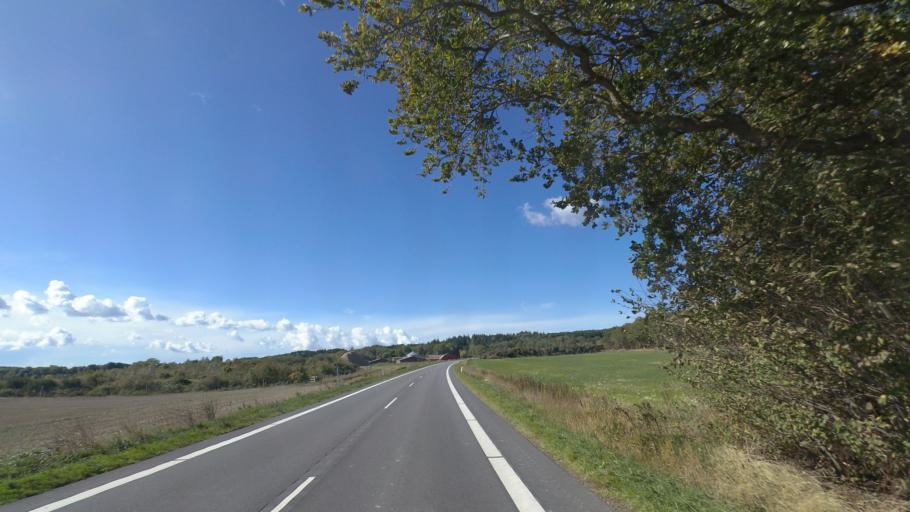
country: DK
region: Capital Region
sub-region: Bornholm Kommune
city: Nexo
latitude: 55.0630
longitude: 15.0274
